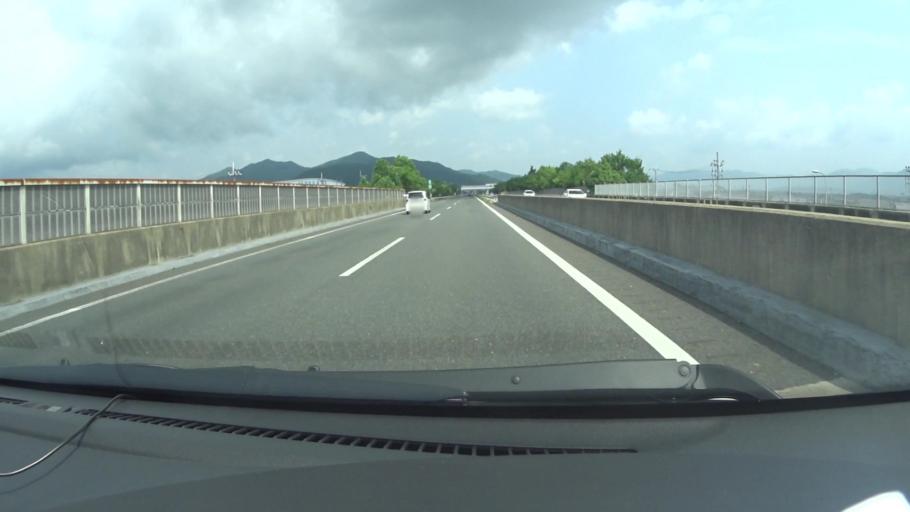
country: JP
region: Kyoto
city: Kameoka
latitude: 35.0108
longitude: 135.5593
